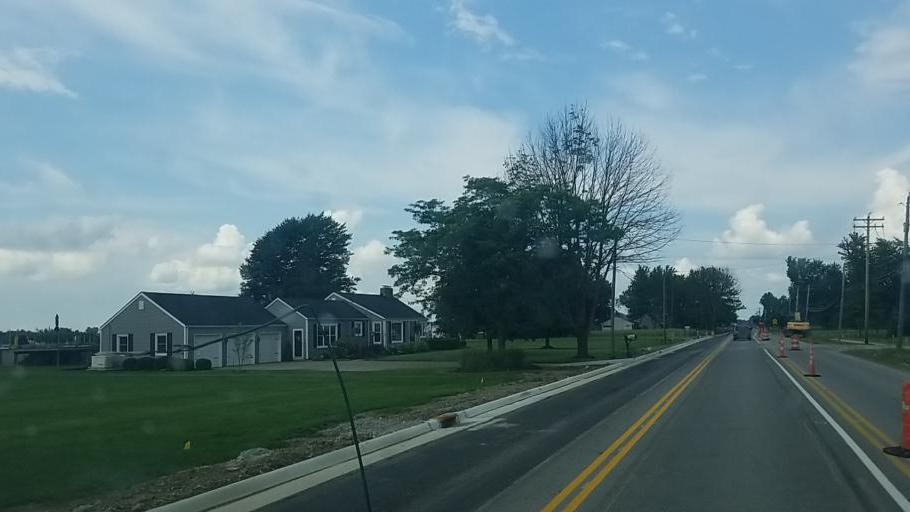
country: US
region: Ohio
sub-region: Lorain County
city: Lagrange
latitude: 41.2484
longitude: -82.1197
